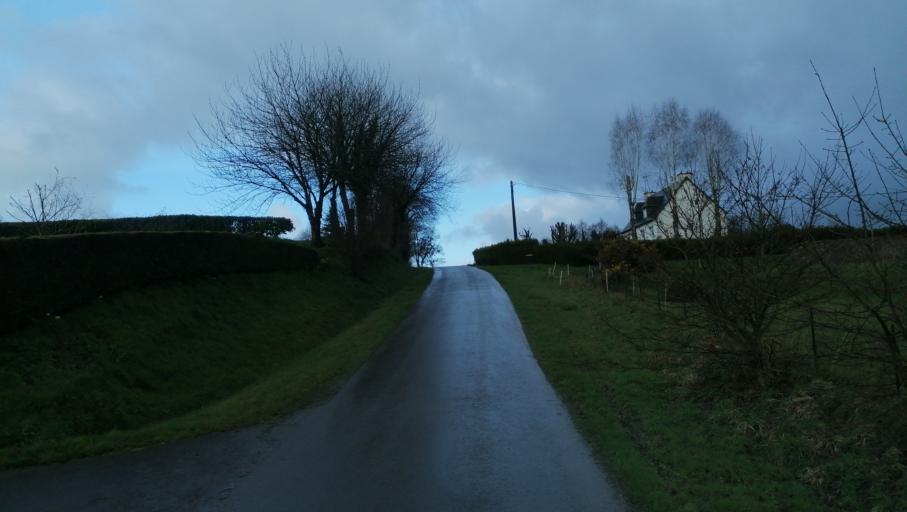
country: FR
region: Brittany
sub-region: Departement des Cotes-d'Armor
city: Plouagat
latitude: 48.4978
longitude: -2.9691
